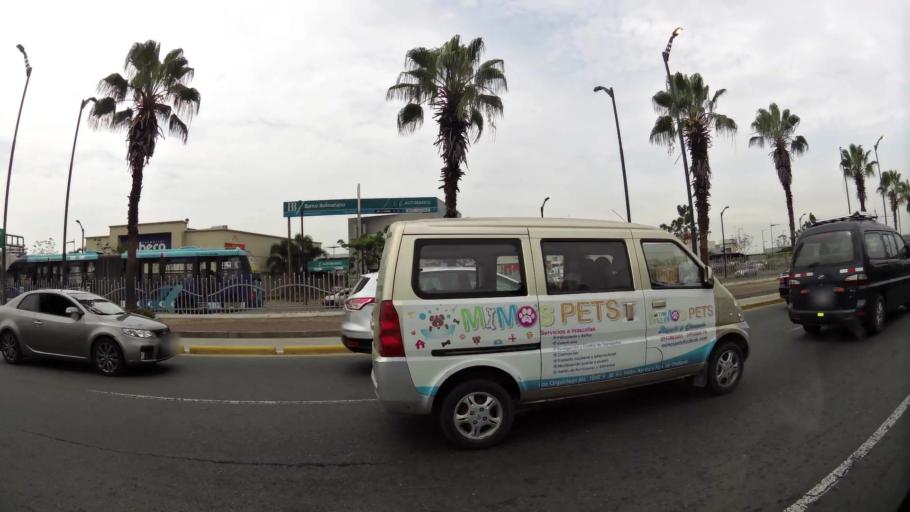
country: EC
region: Guayas
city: Eloy Alfaro
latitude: -2.1491
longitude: -79.8866
